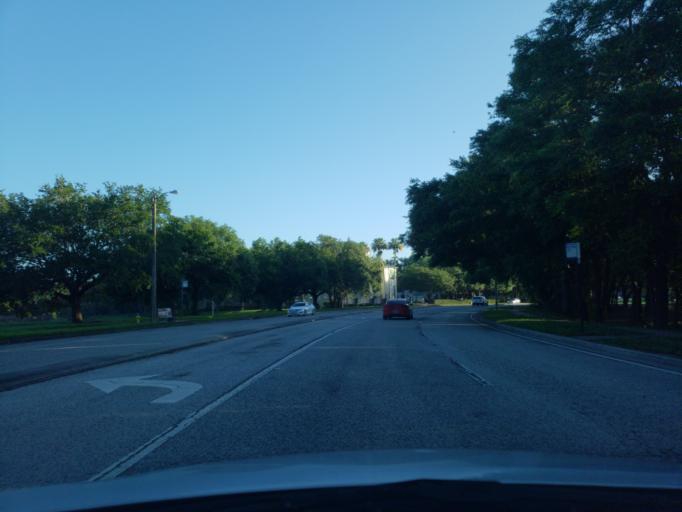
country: US
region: Florida
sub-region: Hillsborough County
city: Mango
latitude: 27.9450
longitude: -82.3262
